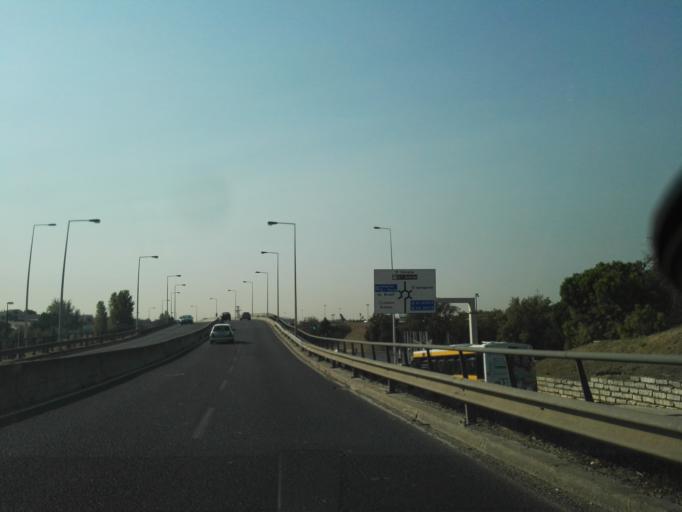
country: PT
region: Lisbon
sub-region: Loures
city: Moscavide
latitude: 38.7630
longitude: -9.1279
